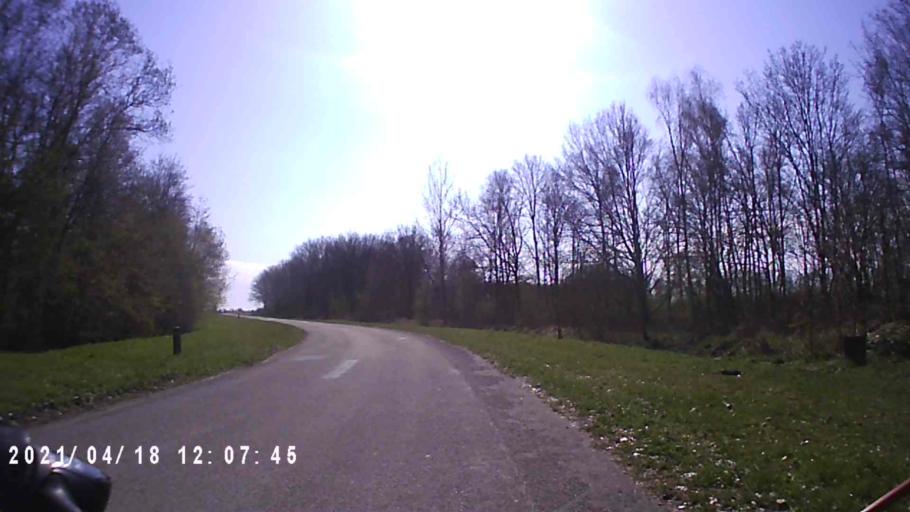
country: NL
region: Friesland
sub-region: Gemeente Kollumerland en Nieuwkruisland
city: Kollum
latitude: 53.3242
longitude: 6.1879
